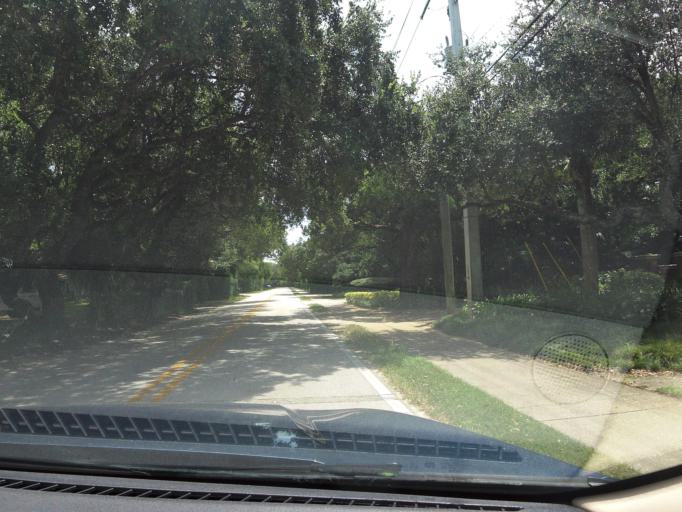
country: US
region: Florida
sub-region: Volusia County
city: Ponce Inlet
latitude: 29.0870
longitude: -80.9338
